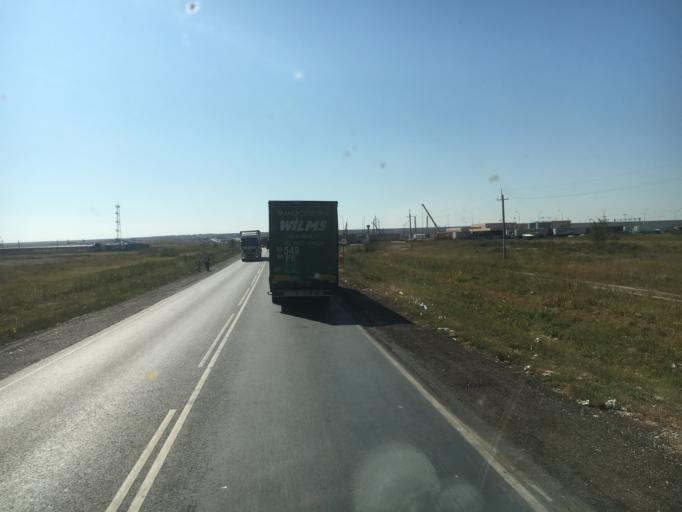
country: KZ
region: Batys Qazaqstan
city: Peremetnoe
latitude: 51.6828
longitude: 51.0031
